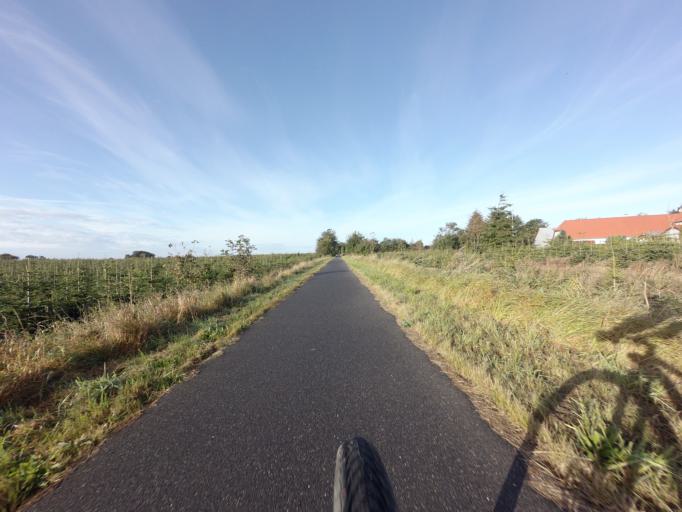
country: DK
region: Central Jutland
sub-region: Viborg Kommune
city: Bjerringbro
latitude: 56.4919
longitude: 9.6550
